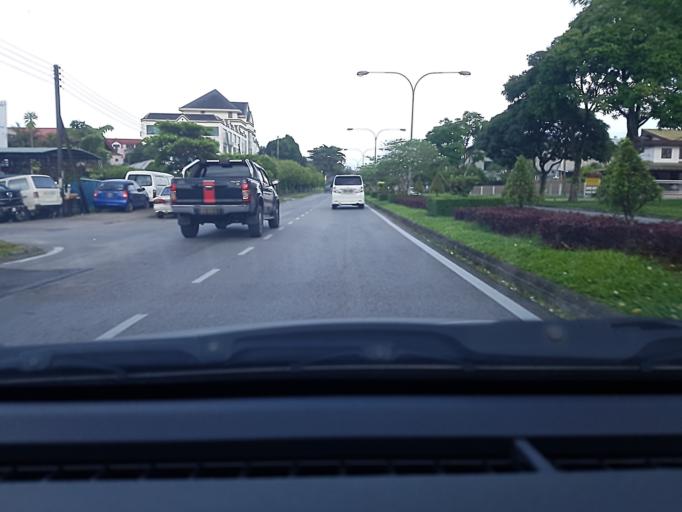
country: MY
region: Sarawak
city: Kuching
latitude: 1.5289
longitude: 110.3630
